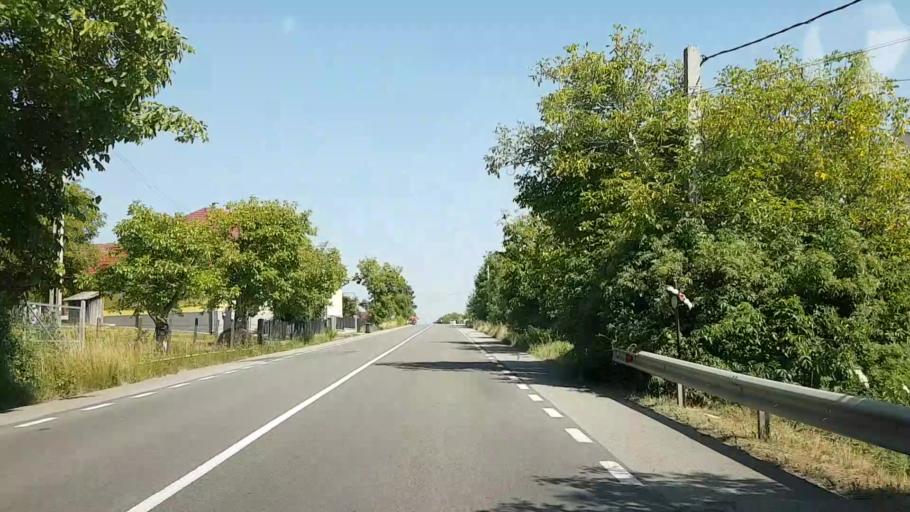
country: RO
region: Bistrita-Nasaud
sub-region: Comuna Uriu
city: Cristestii Ciceului
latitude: 47.1849
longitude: 24.1255
